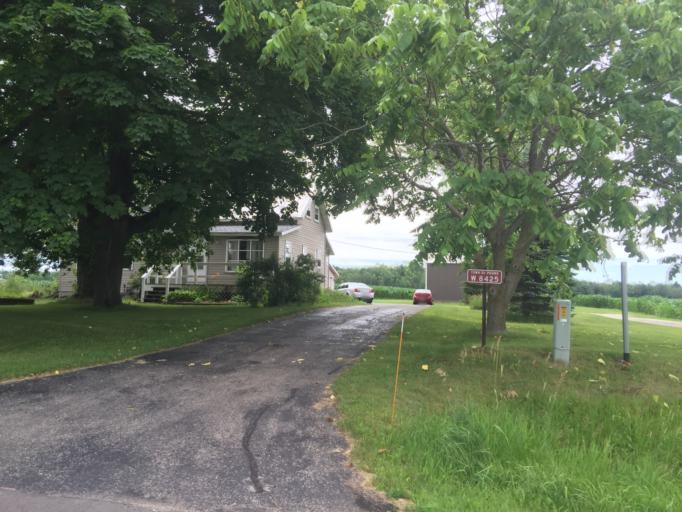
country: US
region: Wisconsin
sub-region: Oconto County
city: Oconto Falls
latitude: 45.0651
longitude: -88.0196
